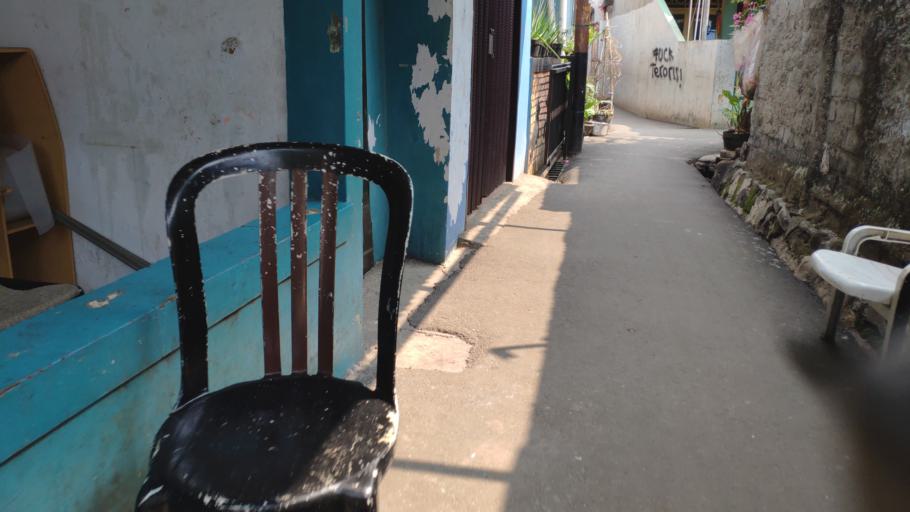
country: ID
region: West Java
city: Depok
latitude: -6.3078
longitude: 106.8283
